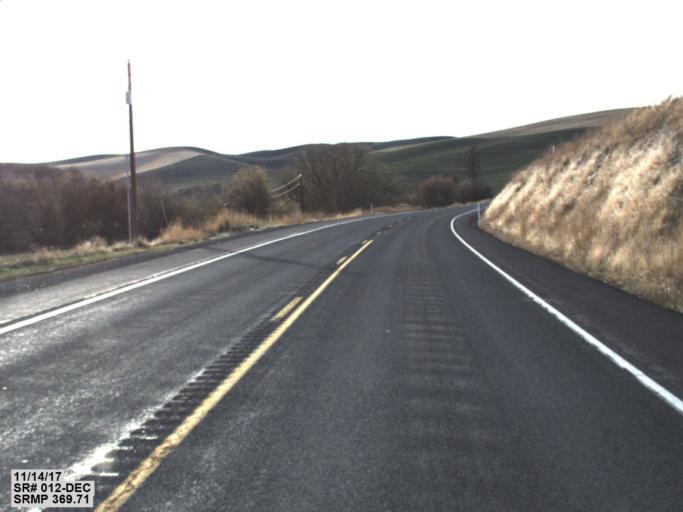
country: US
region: Washington
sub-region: Columbia County
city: Dayton
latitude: 46.3493
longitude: -117.9706
